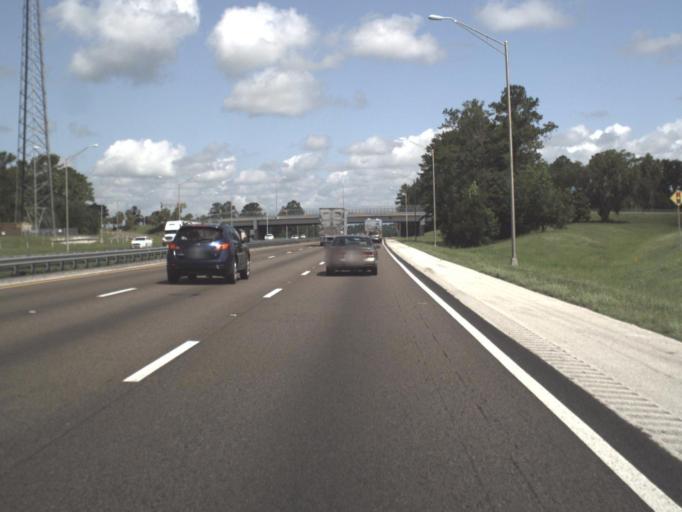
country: US
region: Florida
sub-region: Alachua County
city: Alachua
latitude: 29.6867
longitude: -82.4441
